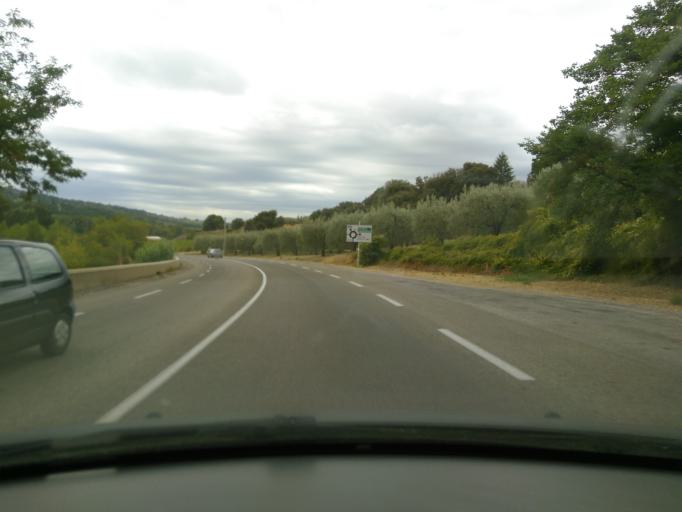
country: FR
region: Rhone-Alpes
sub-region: Departement de la Drome
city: Nyons
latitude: 44.3524
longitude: 5.1156
